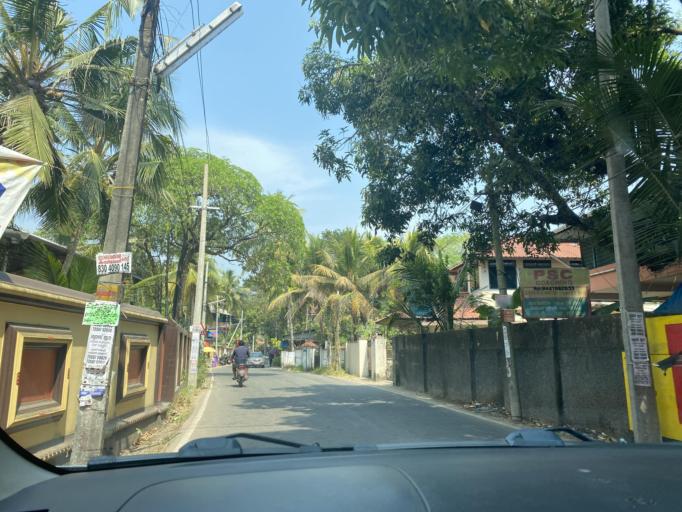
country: IN
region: Kerala
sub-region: Alappuzha
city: Arukutti
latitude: 9.9040
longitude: 76.3212
